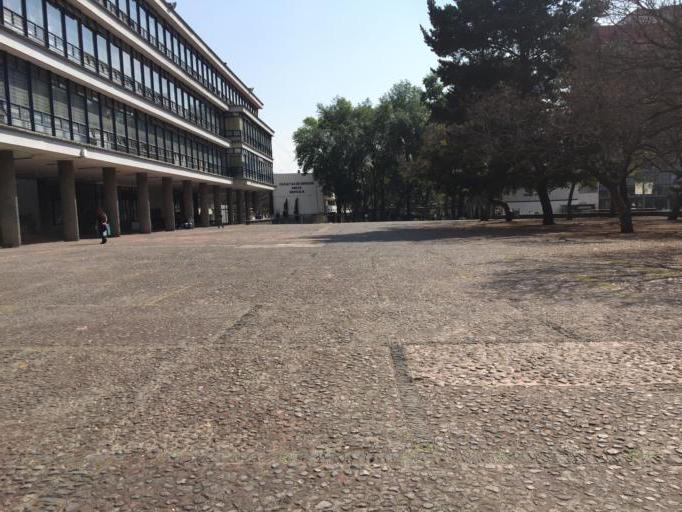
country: MX
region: Mexico City
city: Magdalena Contreras
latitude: 19.3340
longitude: -99.1849
